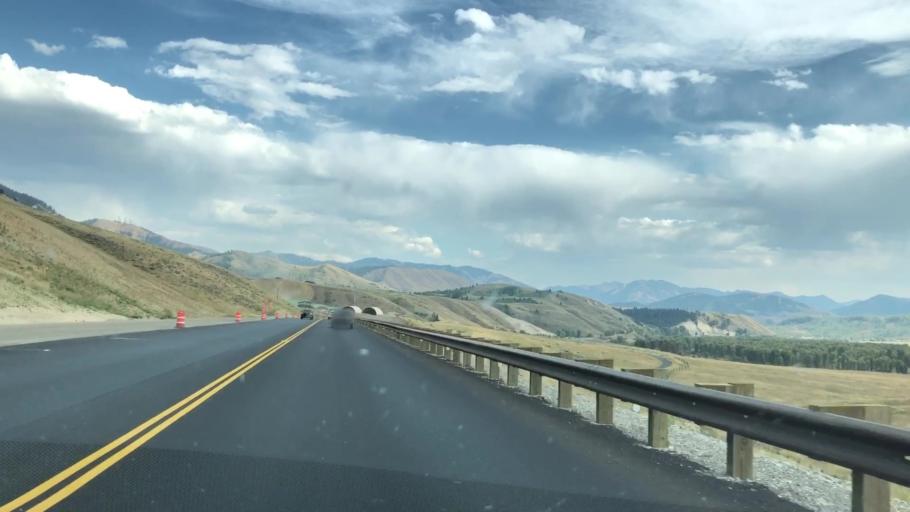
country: US
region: Wyoming
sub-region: Teton County
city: South Park
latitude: 43.4078
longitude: -110.7645
